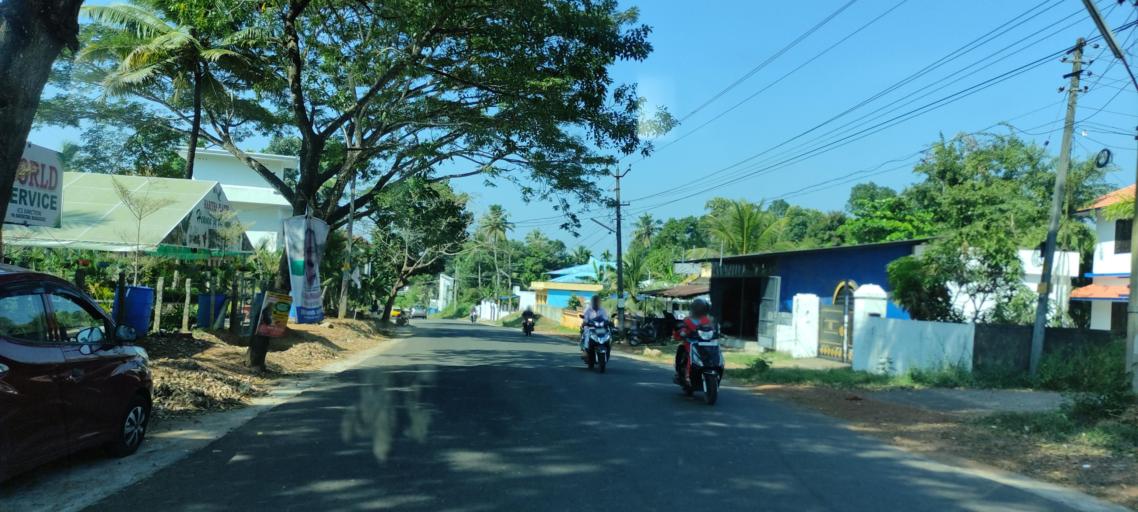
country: IN
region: Kerala
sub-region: Kollam
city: Panmana
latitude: 9.0421
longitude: 76.6092
